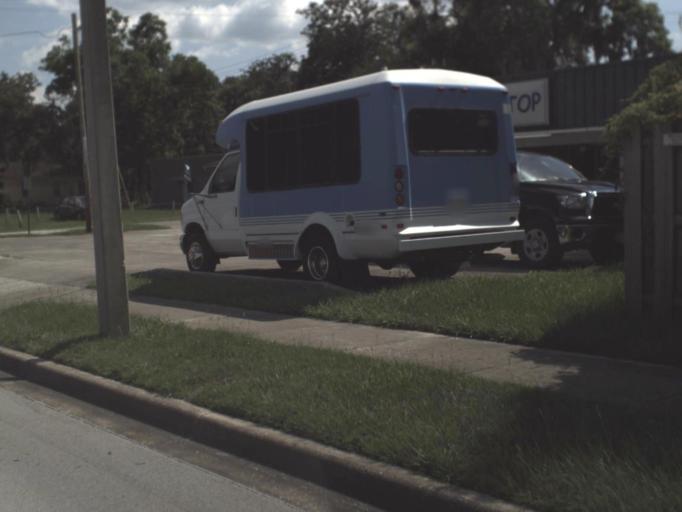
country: US
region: Florida
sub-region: Alachua County
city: Hawthorne
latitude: 29.5891
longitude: -82.0847
